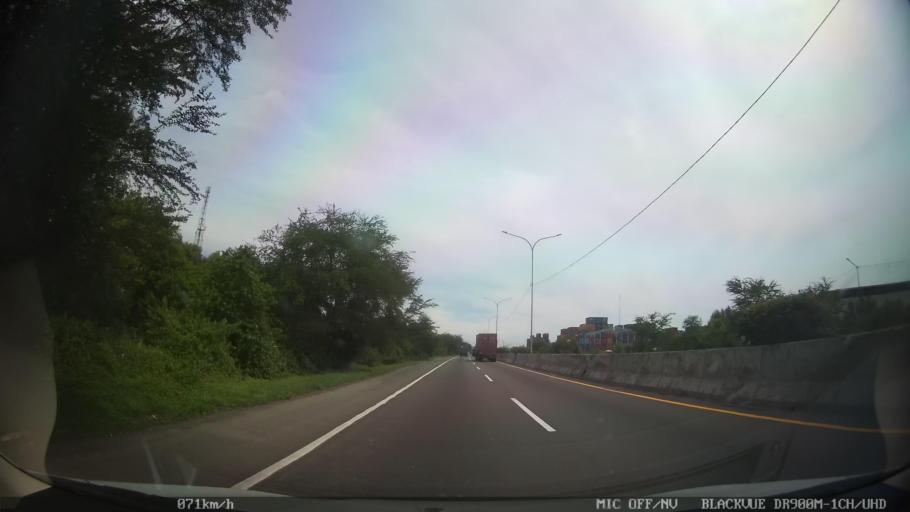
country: ID
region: North Sumatra
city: Belawan
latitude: 3.7647
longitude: 98.6846
